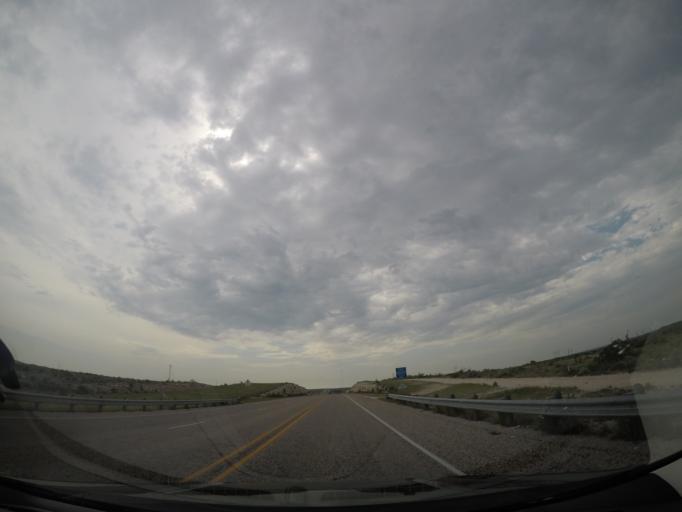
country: US
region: Texas
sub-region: Val Verde County
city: Cienegas Terrace
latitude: 29.7010
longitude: -101.2059
